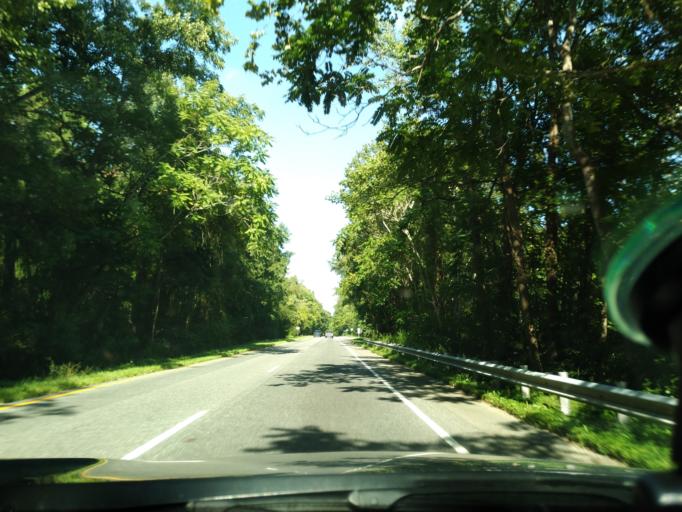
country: US
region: Virginia
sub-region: King George County
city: King George
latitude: 38.1540
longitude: -77.2108
